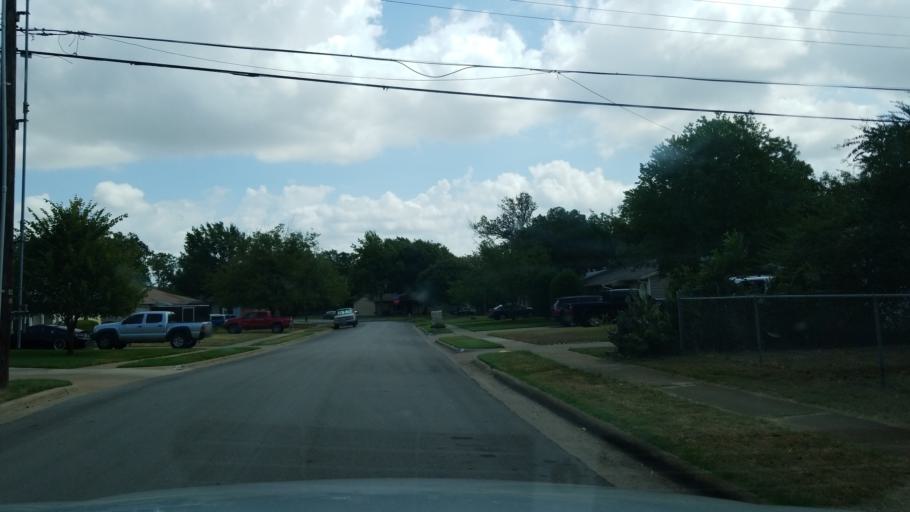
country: US
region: Texas
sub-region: Tarrant County
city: Euless
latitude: 32.8465
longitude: -97.0899
